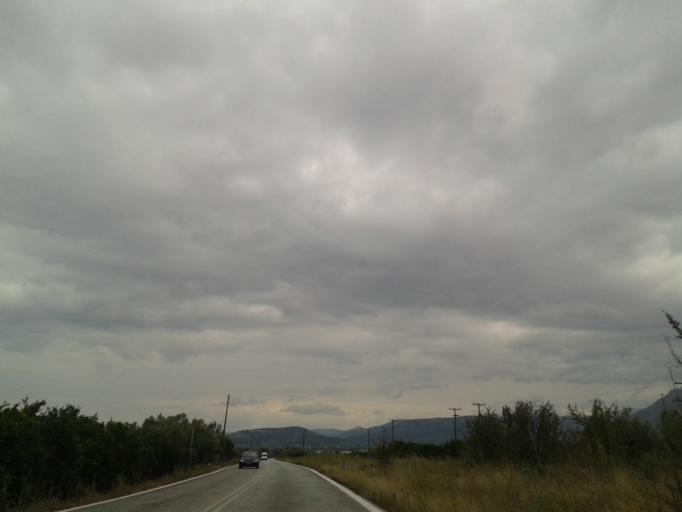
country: GR
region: Peloponnese
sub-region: Nomos Argolidos
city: Koutsopodi
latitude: 37.7010
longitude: 22.7231
